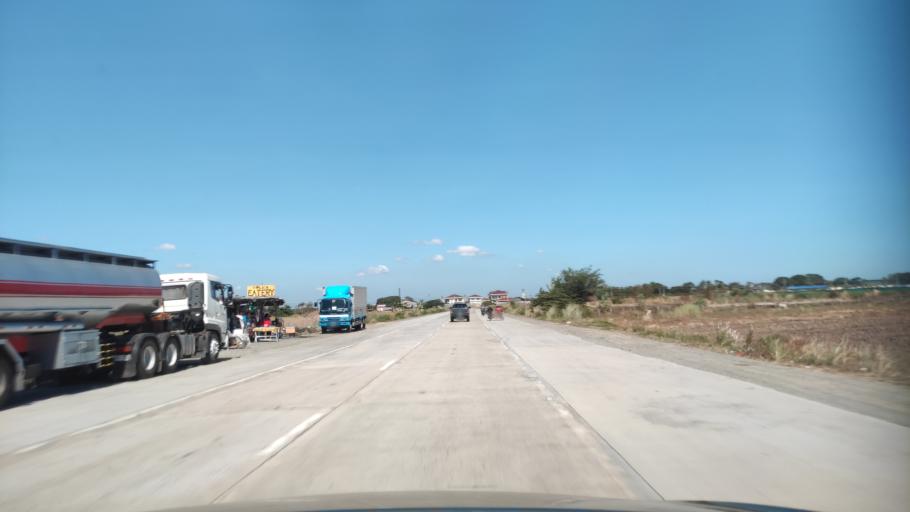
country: PH
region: Central Luzon
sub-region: Province of Tarlac
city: Salcedo
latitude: 15.8702
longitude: 120.6082
